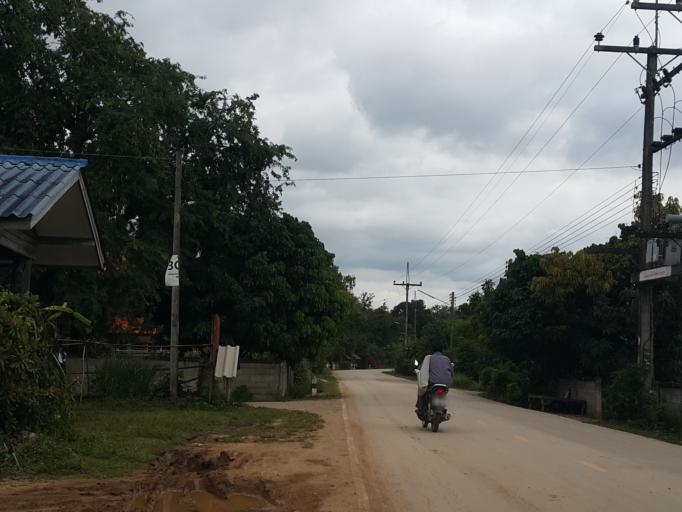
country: TH
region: Lampang
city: Chae Hom
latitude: 18.5742
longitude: 99.4550
